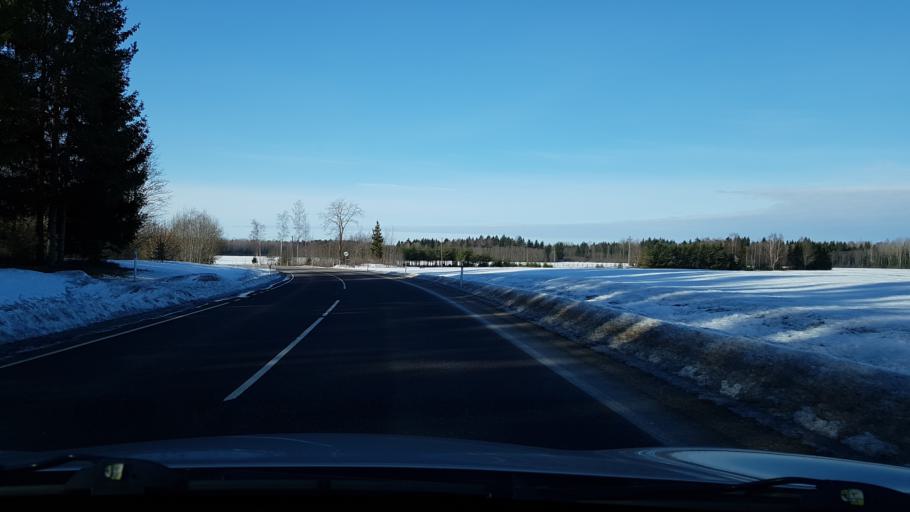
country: EE
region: Jogevamaa
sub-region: Poltsamaa linn
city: Poltsamaa
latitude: 58.6384
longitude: 25.7645
